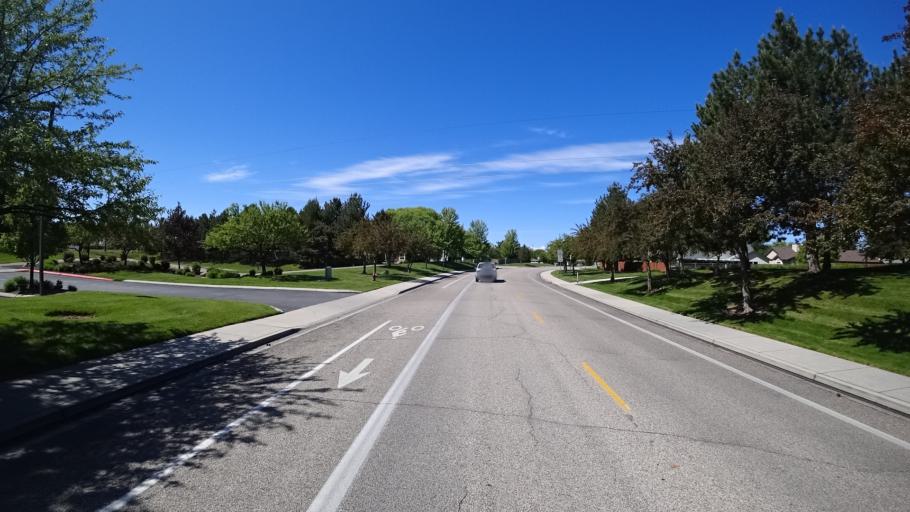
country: US
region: Idaho
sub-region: Ada County
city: Boise
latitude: 43.5497
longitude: -116.1387
